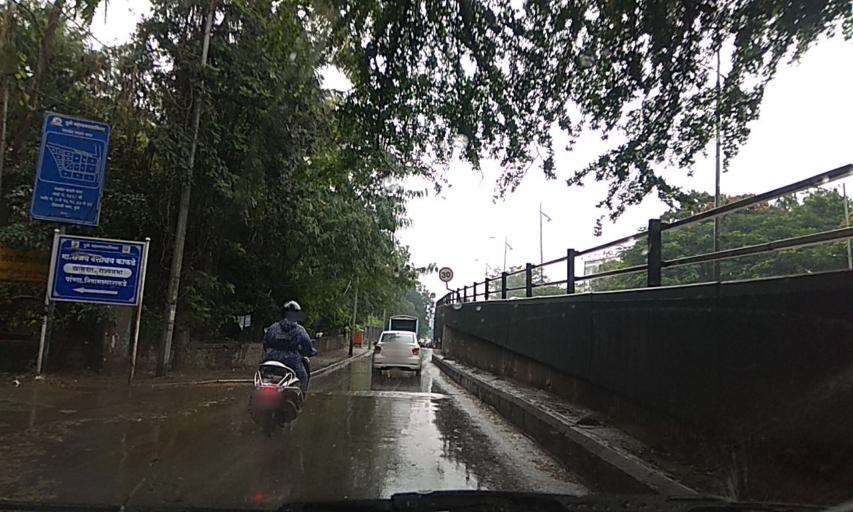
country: IN
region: Maharashtra
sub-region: Pune Division
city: Shivaji Nagar
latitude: 18.5394
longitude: 73.8330
